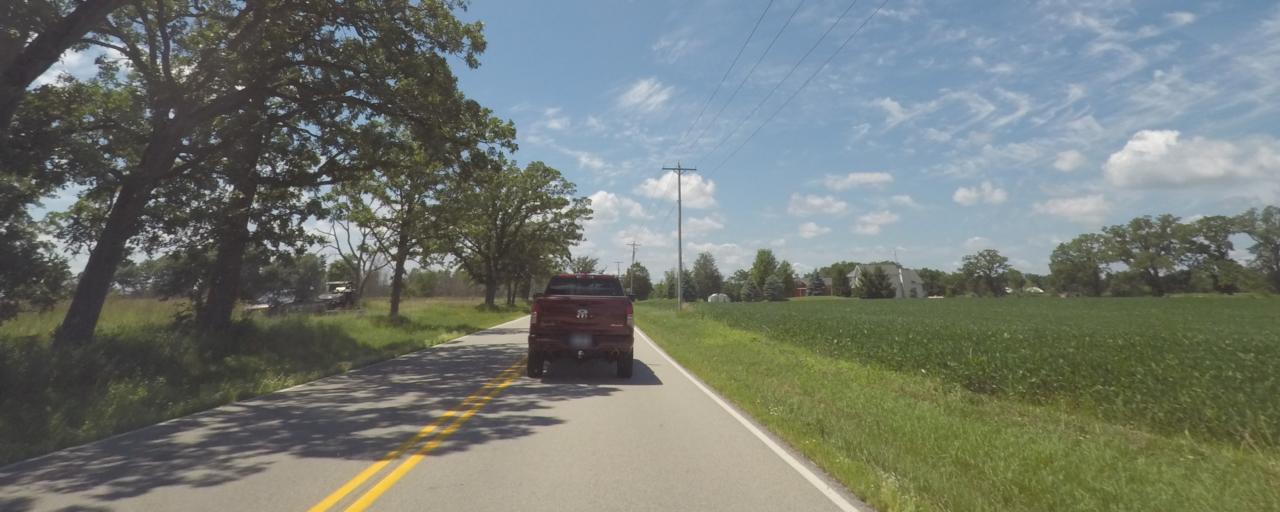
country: US
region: Wisconsin
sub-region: Waukesha County
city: Eagle
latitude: 42.9264
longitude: -88.5273
